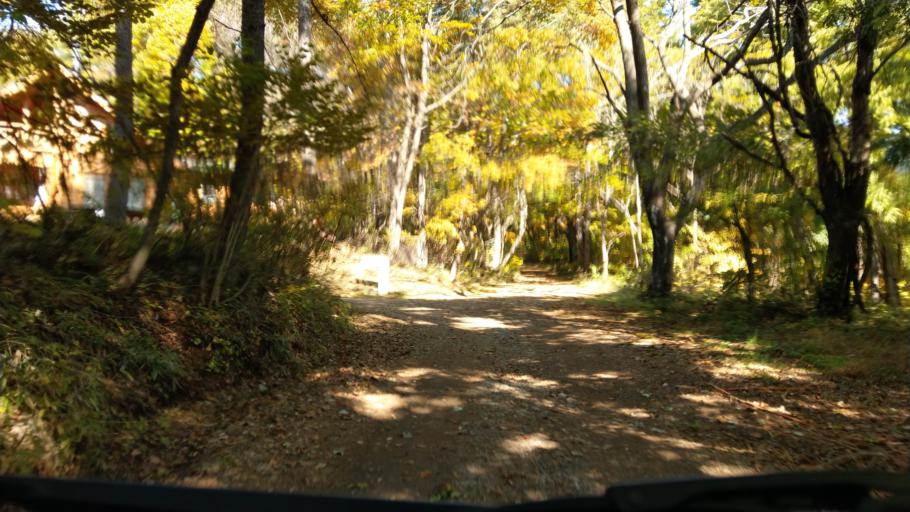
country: JP
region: Nagano
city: Komoro
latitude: 36.3644
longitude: 138.4522
